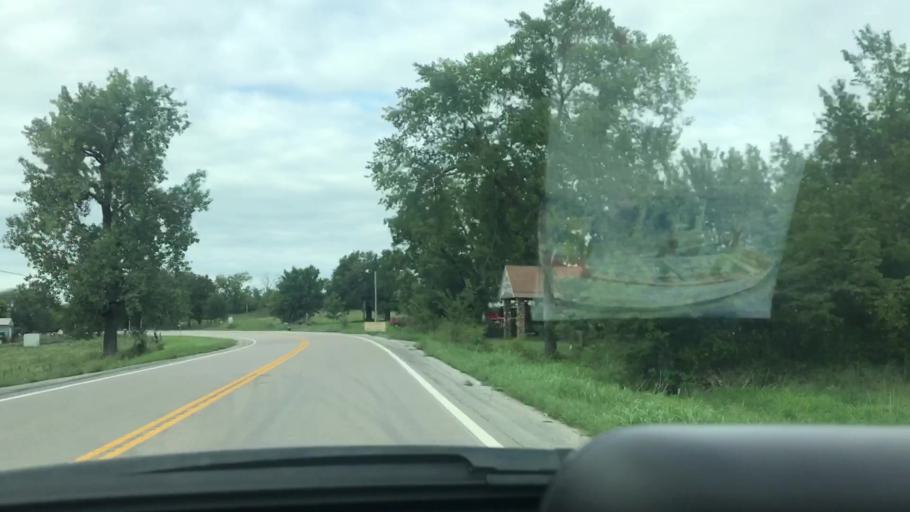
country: US
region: Missouri
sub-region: Benton County
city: Warsaw
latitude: 38.1176
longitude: -93.2758
